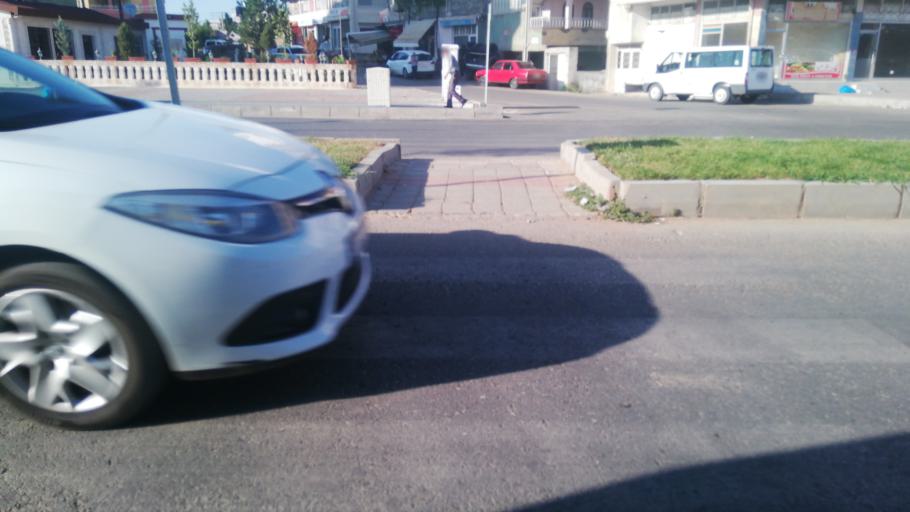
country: TR
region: Mardin
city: Midyat
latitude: 37.4184
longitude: 41.3562
